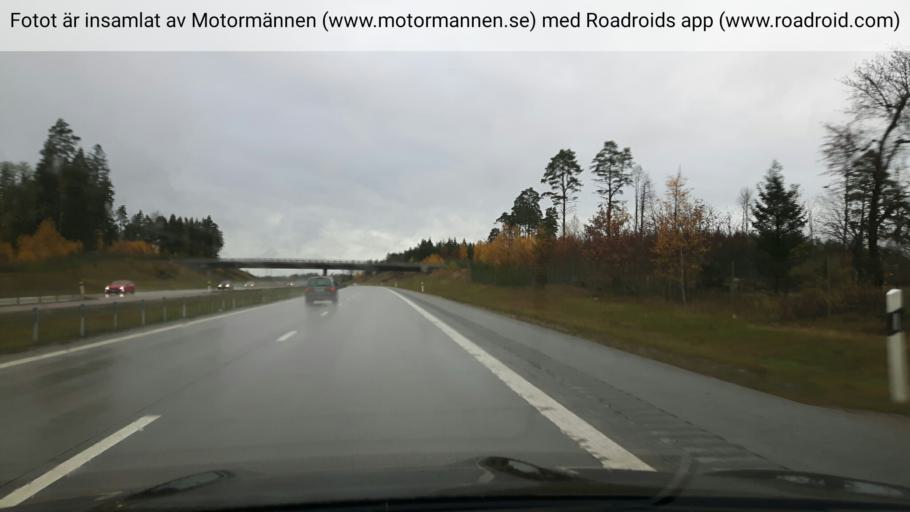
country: SE
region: Uppsala
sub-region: Uppsala Kommun
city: Storvreta
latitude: 59.9642
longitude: 17.6476
